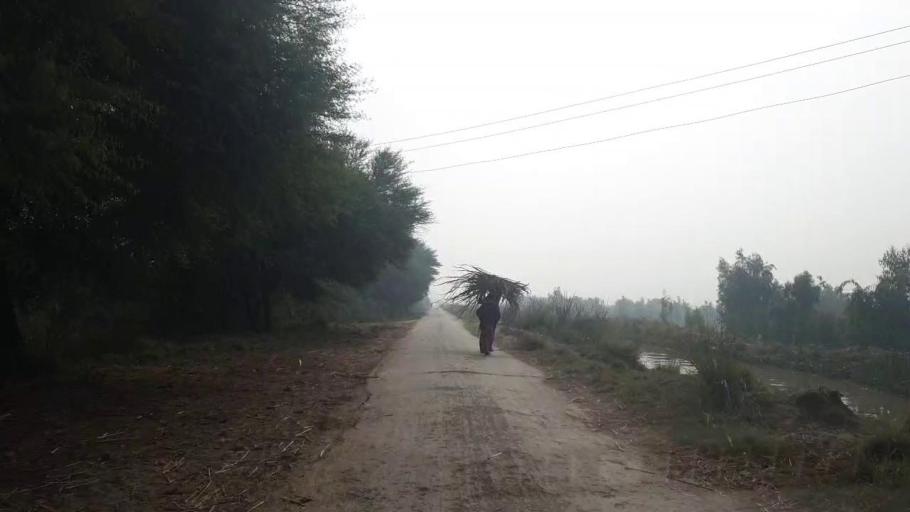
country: PK
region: Sindh
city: Tando Adam
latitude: 25.7639
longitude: 68.6091
